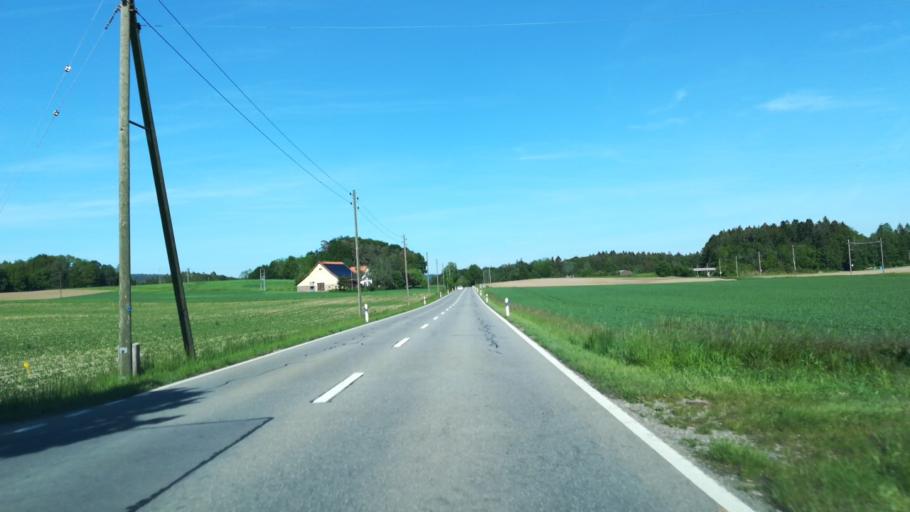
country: CH
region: Thurgau
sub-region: Frauenfeld District
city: Diessenhofen
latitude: 47.6244
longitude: 8.7514
